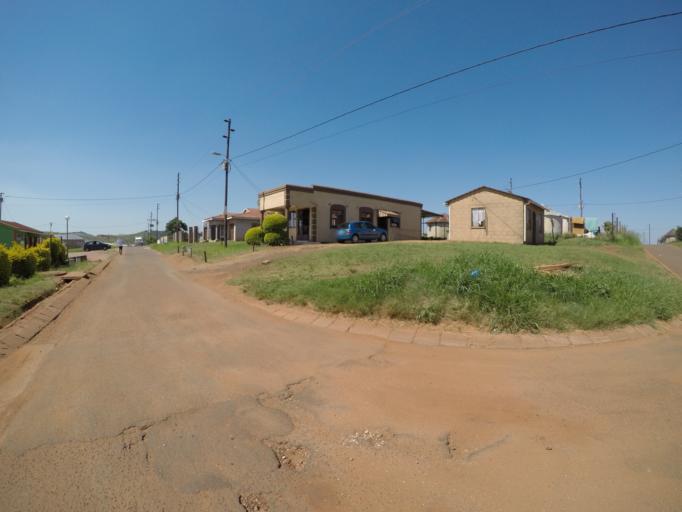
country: ZA
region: KwaZulu-Natal
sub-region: uThungulu District Municipality
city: Empangeni
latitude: -28.7689
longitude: 31.8766
